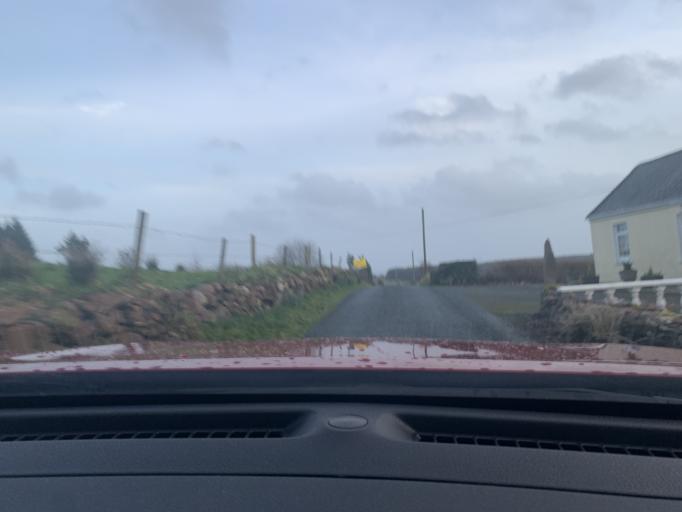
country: IE
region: Connaught
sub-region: Roscommon
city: Ballaghaderreen
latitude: 53.9516
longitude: -8.5211
